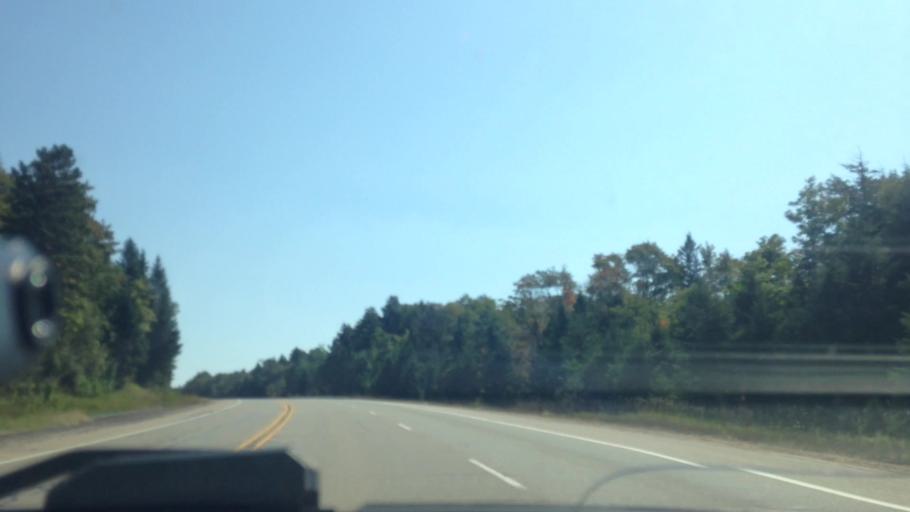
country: US
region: Michigan
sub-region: Alger County
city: Munising
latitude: 46.3888
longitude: -86.6455
